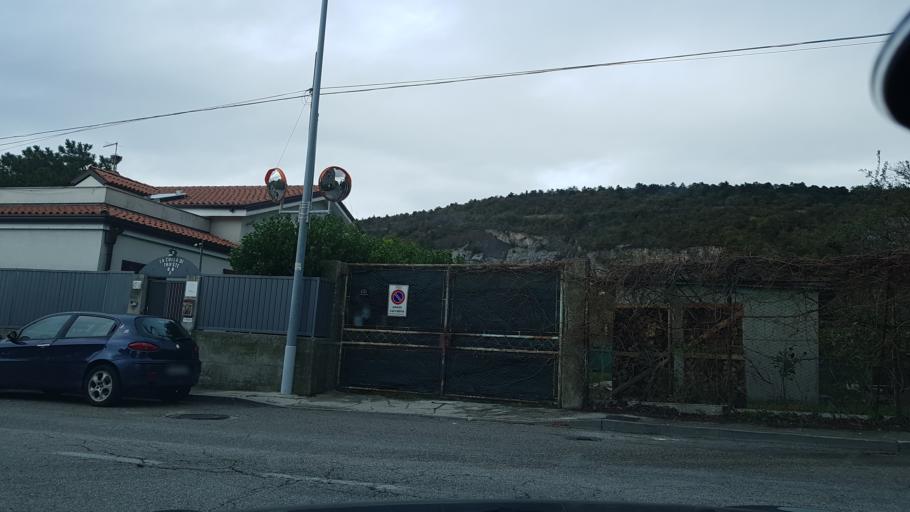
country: IT
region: Friuli Venezia Giulia
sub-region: Provincia di Trieste
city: Domio
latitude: 45.6411
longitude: 13.8253
